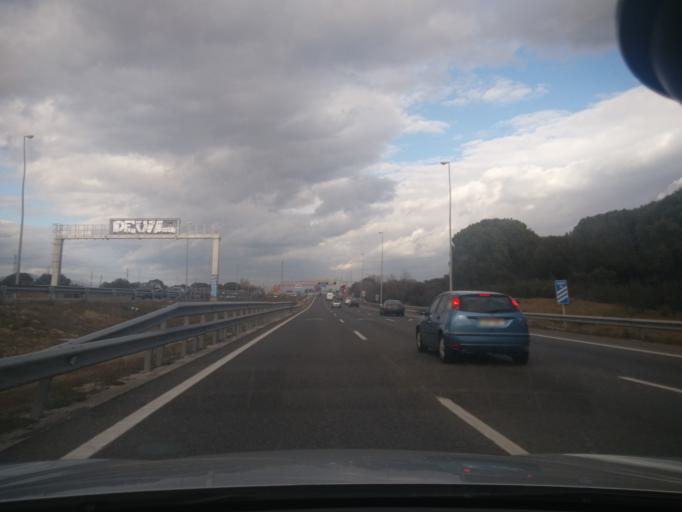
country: ES
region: Madrid
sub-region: Provincia de Madrid
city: Tres Cantos
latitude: 40.5746
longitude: -3.7083
